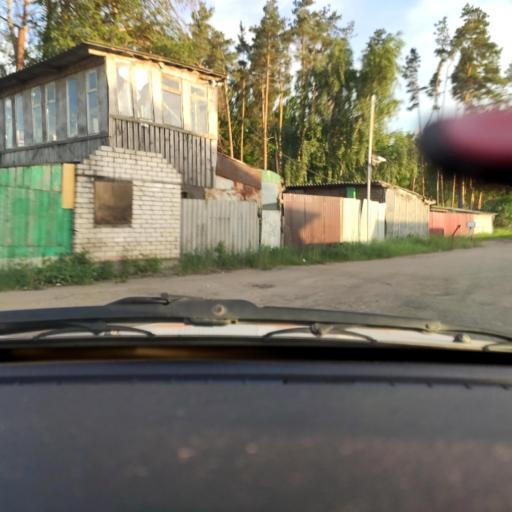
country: RU
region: Voronezj
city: Podgornoye
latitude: 51.8373
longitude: 39.2005
